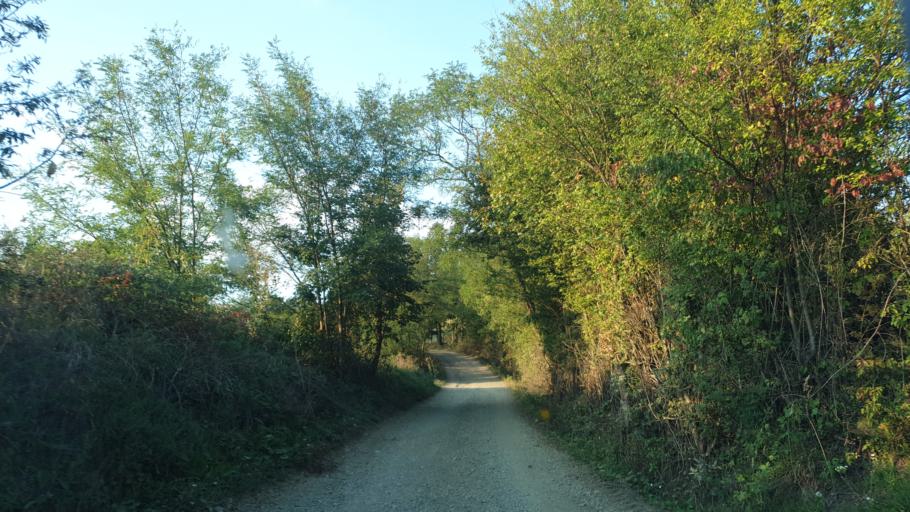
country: RS
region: Central Serbia
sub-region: Zlatiborski Okrug
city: Kosjeric
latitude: 43.9964
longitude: 20.0032
